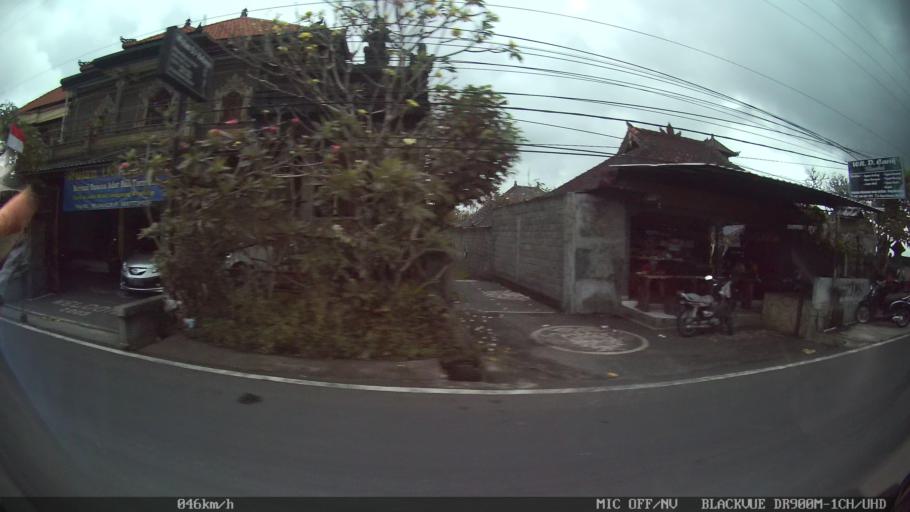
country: ID
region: Bali
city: Banjar Mambalkajanan
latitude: -8.5437
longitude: 115.2225
